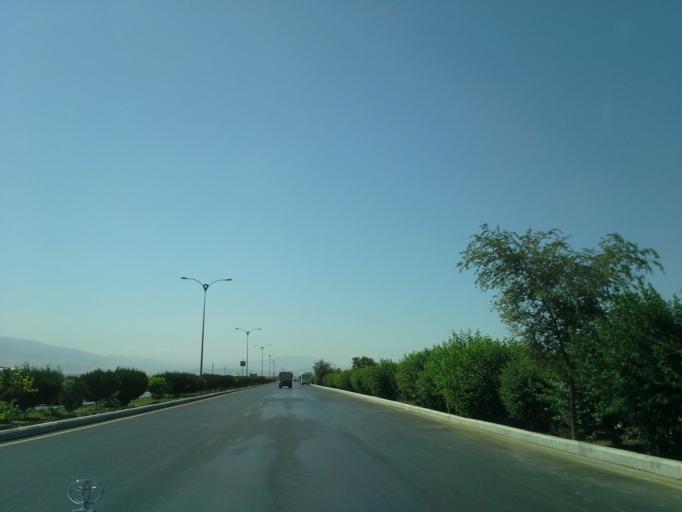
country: TM
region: Ahal
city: Annau
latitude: 37.9063
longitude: 58.5276
